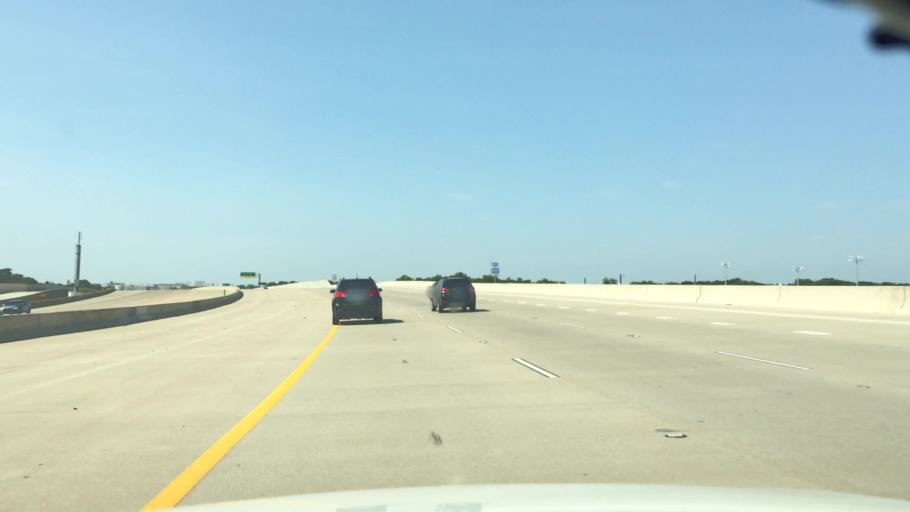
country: US
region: Texas
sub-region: Dallas County
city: Grand Prairie
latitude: 32.7691
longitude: -97.0276
